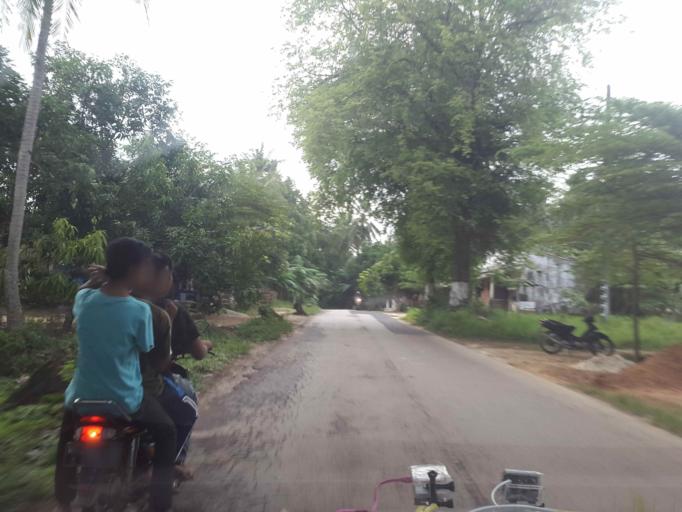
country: ID
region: East Java
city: Giring Barat
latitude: -6.9705
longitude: 113.8659
